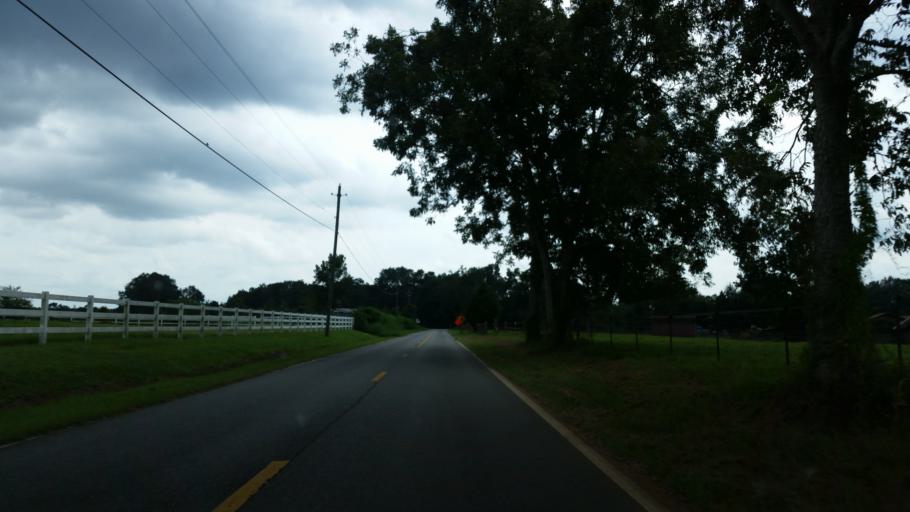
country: US
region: Florida
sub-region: Escambia County
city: Molino
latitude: 30.6937
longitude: -87.4055
